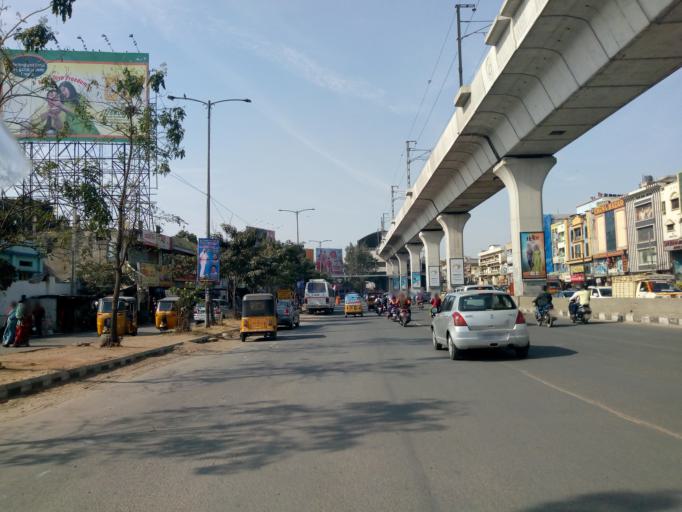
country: IN
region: Telangana
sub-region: Rangareddi
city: Lal Bahadur Nagar
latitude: 17.3478
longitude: 78.5494
